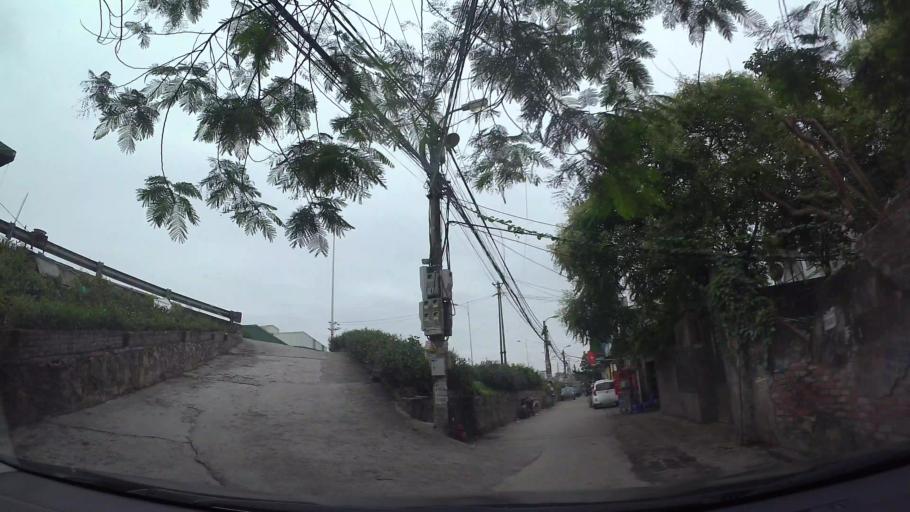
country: VN
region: Ha Noi
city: Hai BaTrung
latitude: 21.0017
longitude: 105.8771
